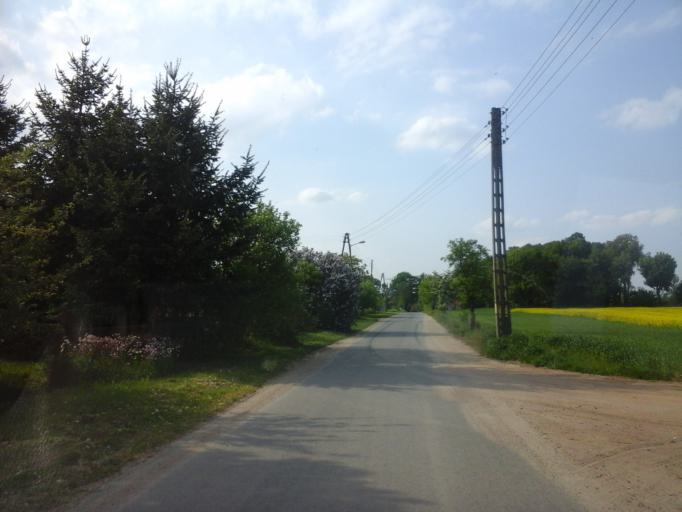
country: PL
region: West Pomeranian Voivodeship
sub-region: Powiat choszczenski
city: Pelczyce
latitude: 53.0441
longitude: 15.2523
